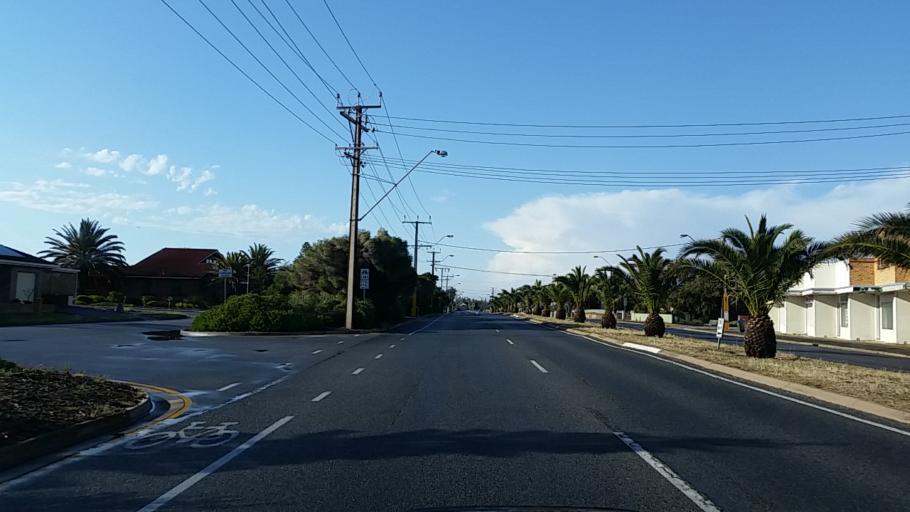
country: AU
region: South Australia
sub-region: Charles Sturt
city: West Lakes Shore
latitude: -34.8611
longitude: 138.4790
